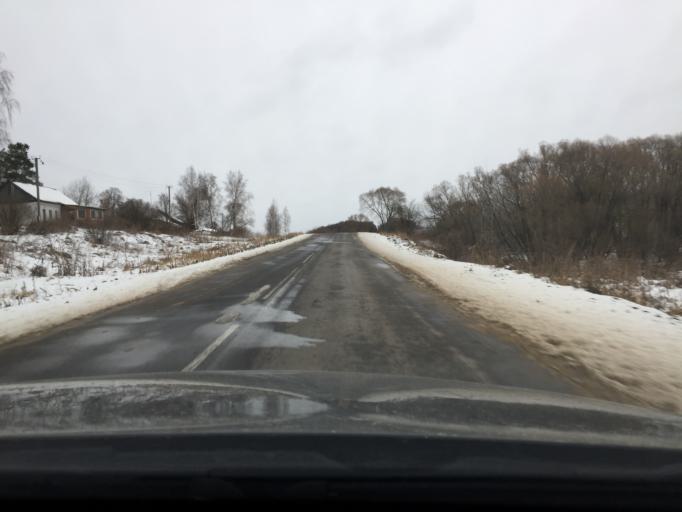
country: RU
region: Tula
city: Shchekino
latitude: 53.8190
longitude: 37.5604
